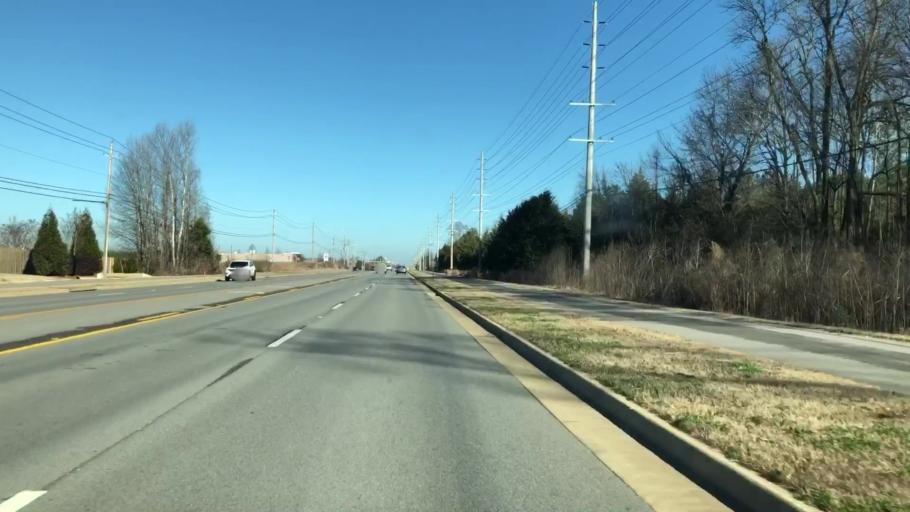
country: US
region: Alabama
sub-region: Madison County
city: Madison
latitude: 34.7248
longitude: -86.7863
